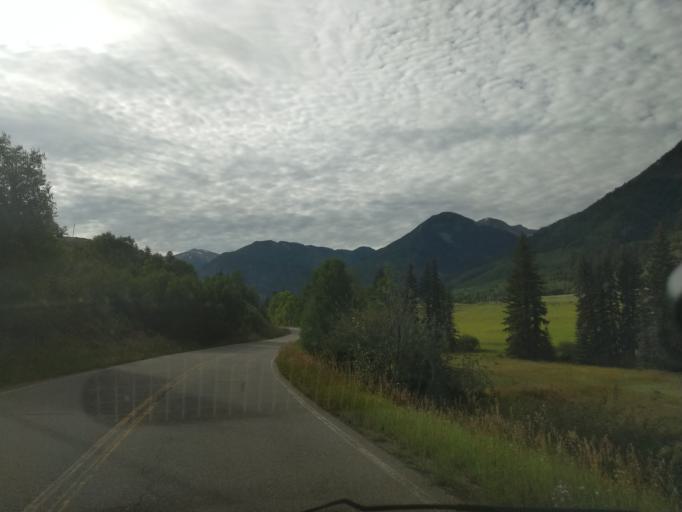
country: US
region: Colorado
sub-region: Garfield County
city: Carbondale
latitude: 39.0848
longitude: -107.2384
